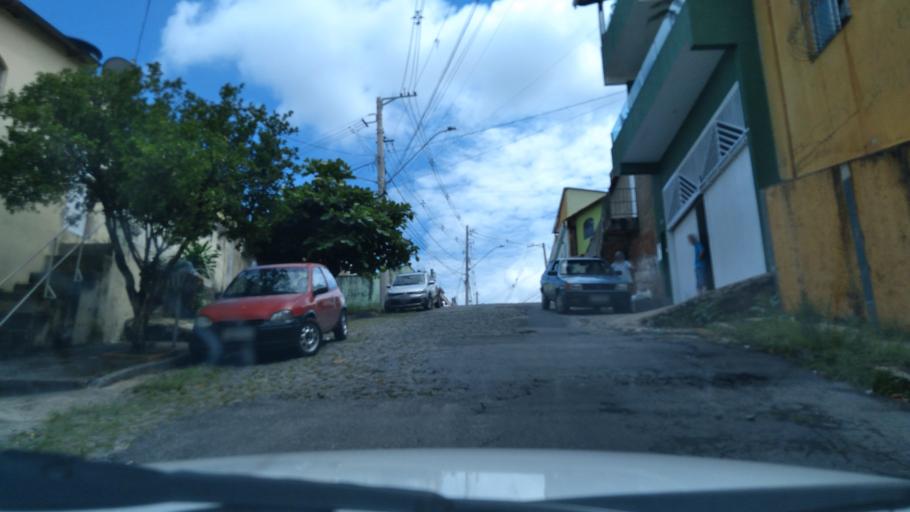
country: BR
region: Minas Gerais
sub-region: Belo Horizonte
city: Belo Horizonte
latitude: -19.8915
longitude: -43.8905
